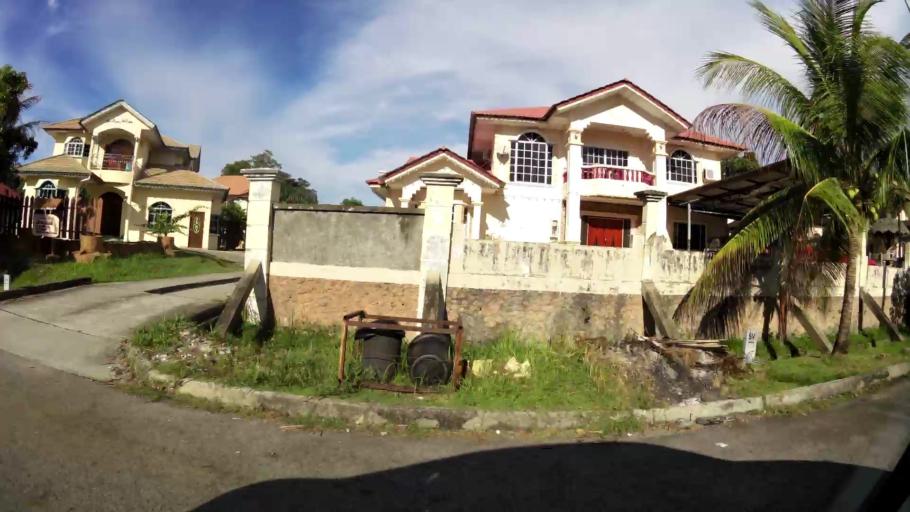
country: BN
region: Brunei and Muara
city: Bandar Seri Begawan
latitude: 4.9840
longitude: 114.9623
